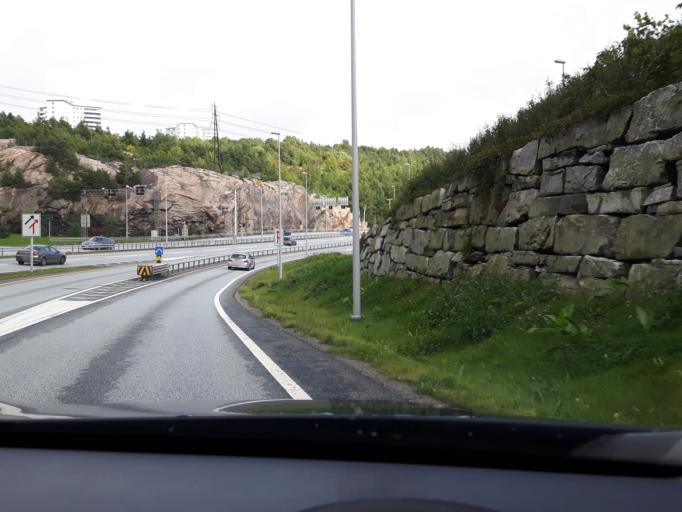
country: NO
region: Vest-Agder
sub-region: Kristiansand
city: Kristiansand
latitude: 58.1399
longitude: 7.9661
